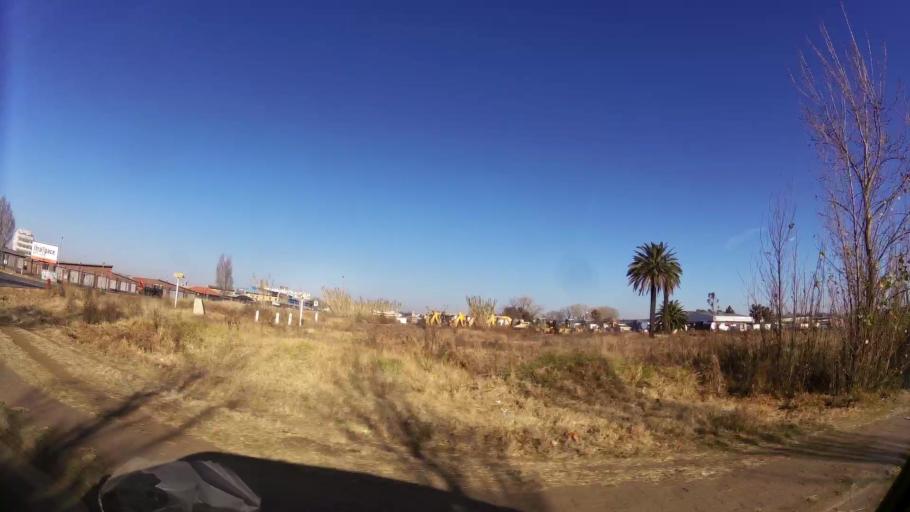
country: ZA
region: Gauteng
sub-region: Ekurhuleni Metropolitan Municipality
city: Germiston
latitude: -26.2892
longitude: 28.1375
